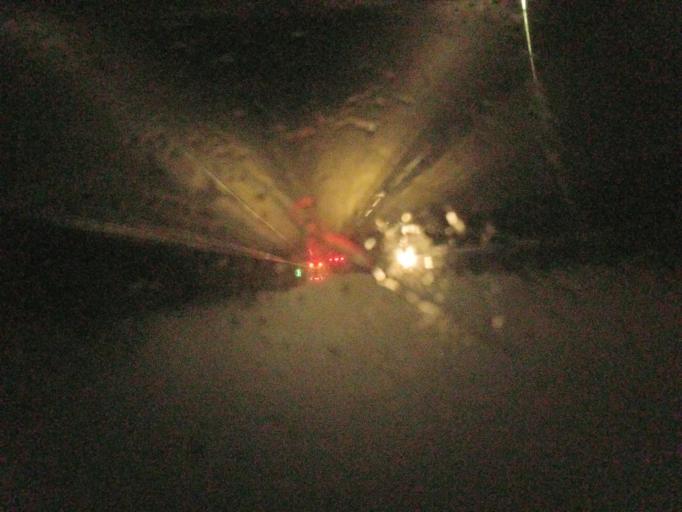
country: US
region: Illinois
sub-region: Fayette County
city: Vandalia
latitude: 38.9768
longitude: -89.0783
